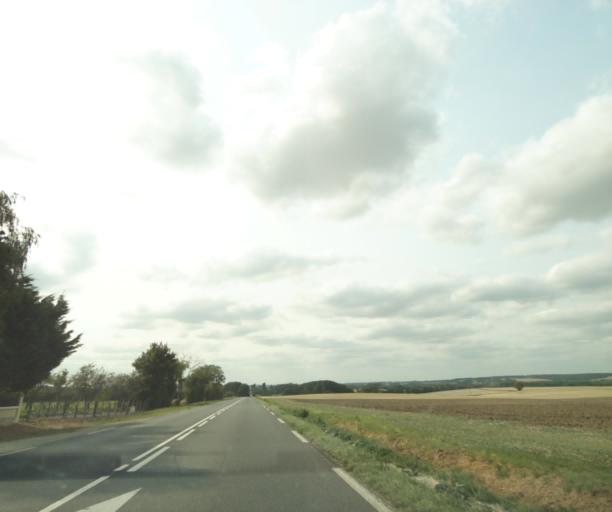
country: FR
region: Centre
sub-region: Departement de l'Indre
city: Clion
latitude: 46.9149
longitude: 1.3220
